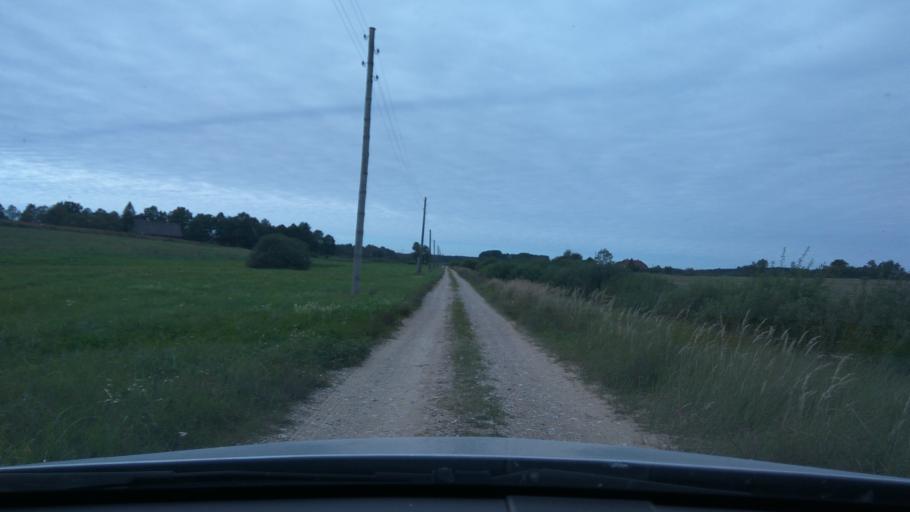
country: LV
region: Kuldigas Rajons
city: Kuldiga
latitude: 57.2416
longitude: 21.9565
